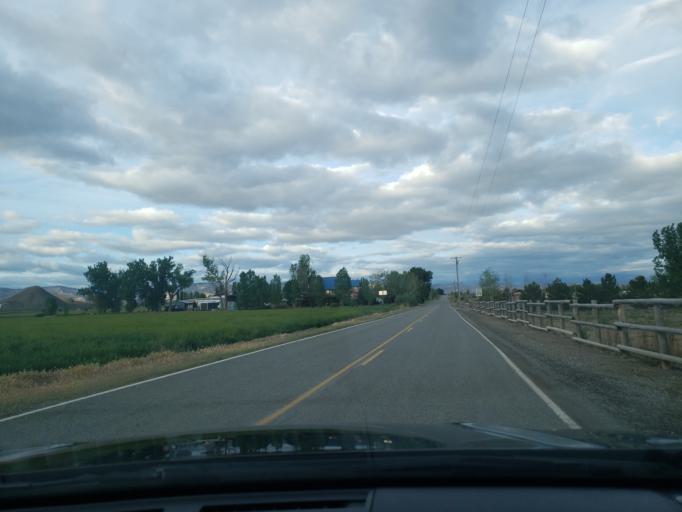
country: US
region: Colorado
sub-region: Mesa County
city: Fruita
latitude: 39.2221
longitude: -108.7196
